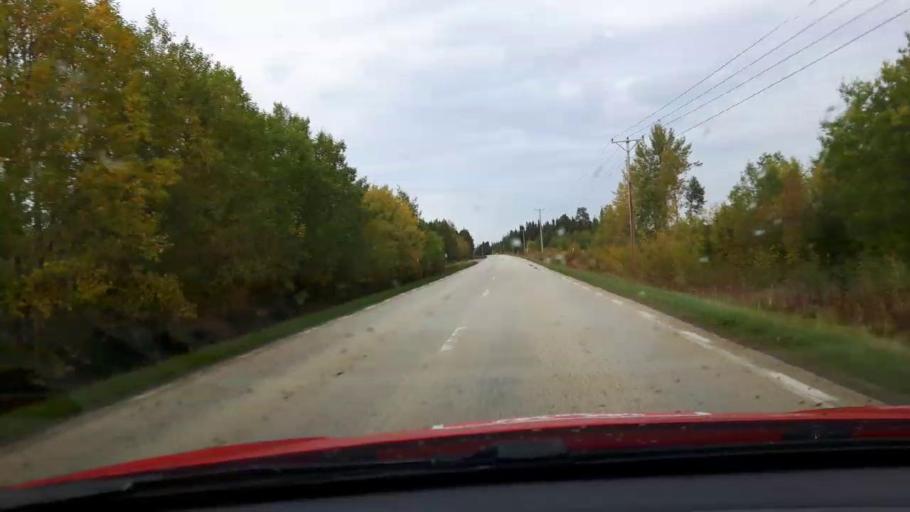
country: SE
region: Jaemtland
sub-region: Bergs Kommun
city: Hoverberg
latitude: 62.9627
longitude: 14.3475
